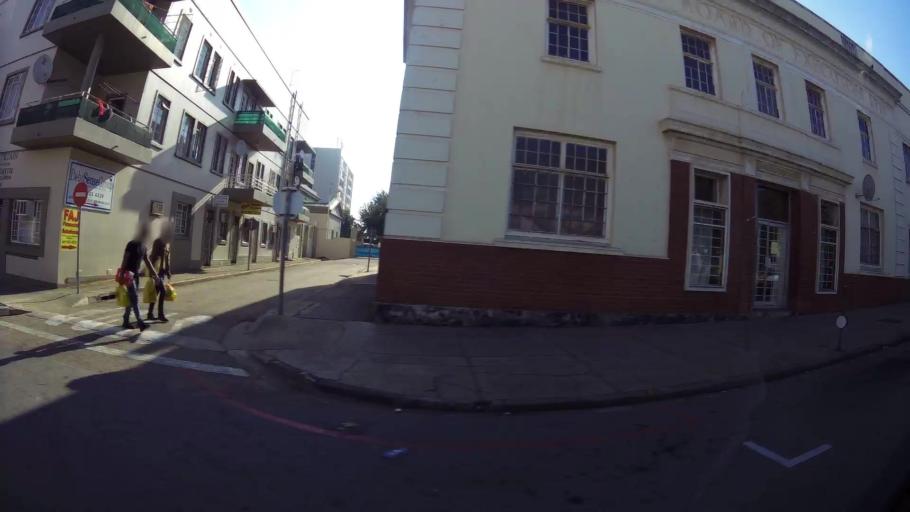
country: ZA
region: Eastern Cape
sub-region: Nelson Mandela Bay Metropolitan Municipality
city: Uitenhage
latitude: -33.7660
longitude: 25.3999
